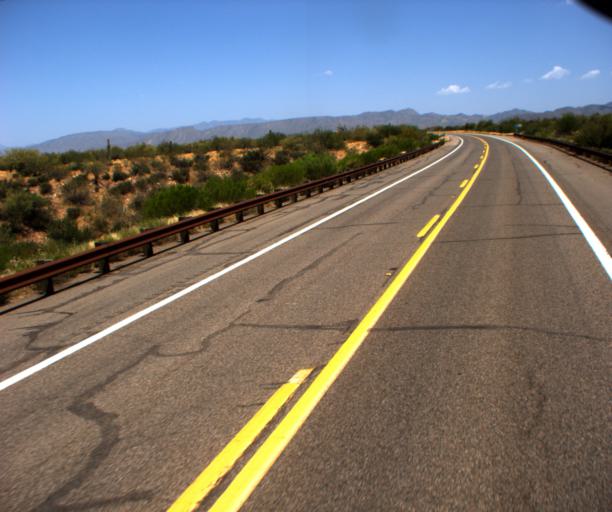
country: US
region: Arizona
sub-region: Gila County
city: Miami
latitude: 33.6205
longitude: -111.0575
